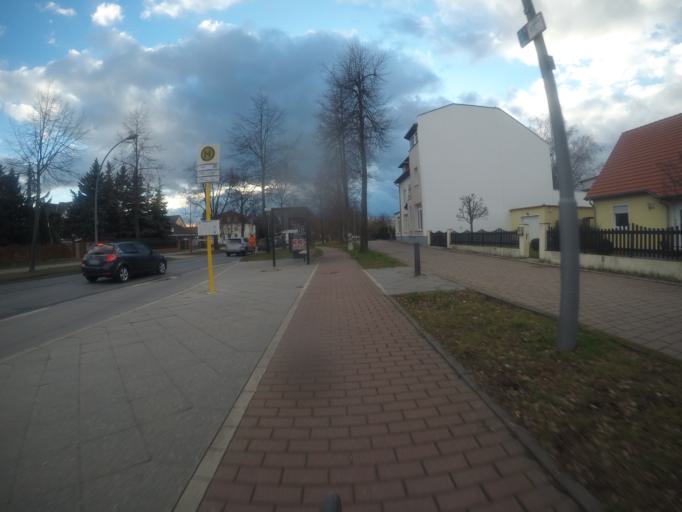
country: DE
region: Berlin
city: Neu-Hohenschoenhausen
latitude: 52.5537
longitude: 13.5207
